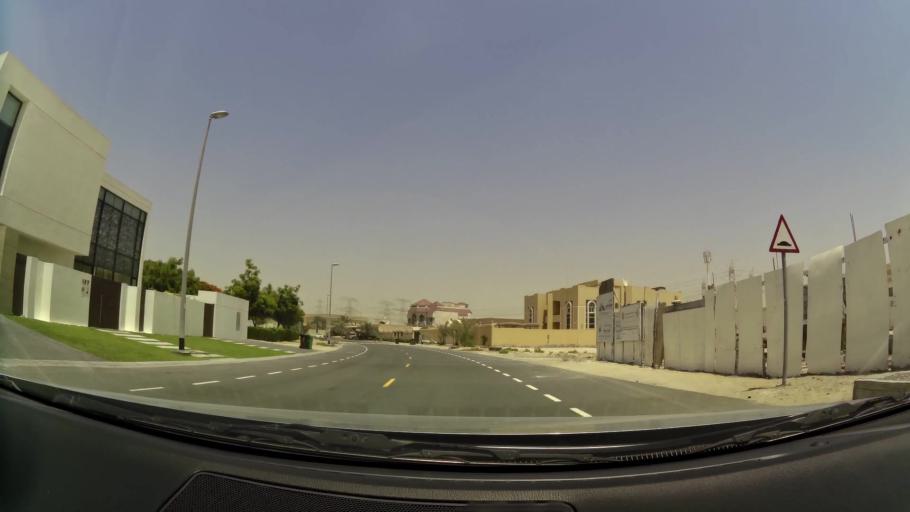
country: AE
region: Dubai
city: Dubai
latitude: 25.0821
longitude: 55.2069
